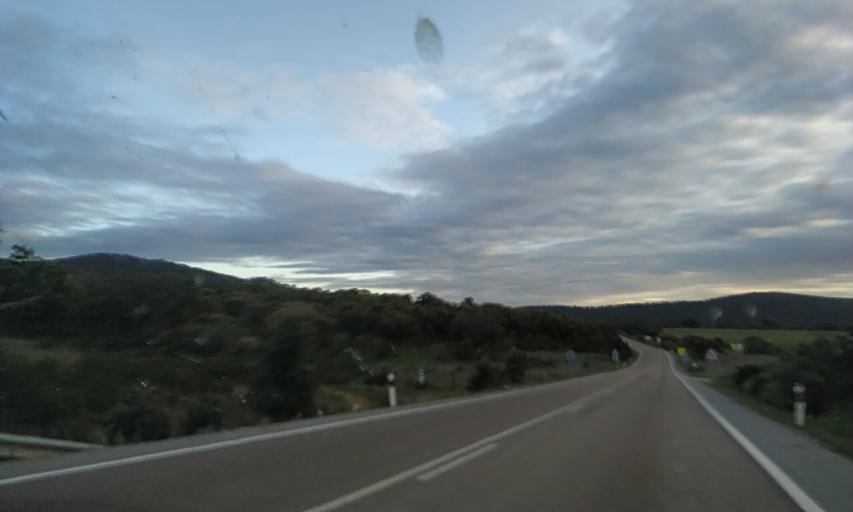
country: ES
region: Extremadura
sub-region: Provincia de Caceres
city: Malpartida de Caceres
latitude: 39.3005
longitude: -6.5164
